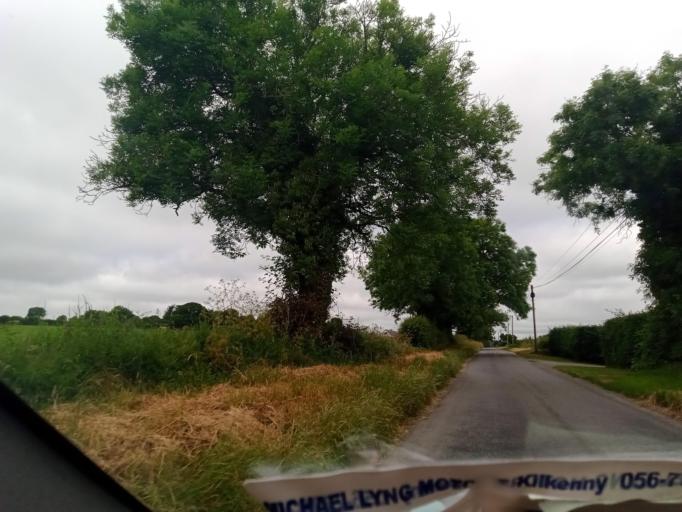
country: IE
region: Leinster
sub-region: Kilkenny
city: Ballyragget
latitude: 52.7537
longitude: -7.4429
